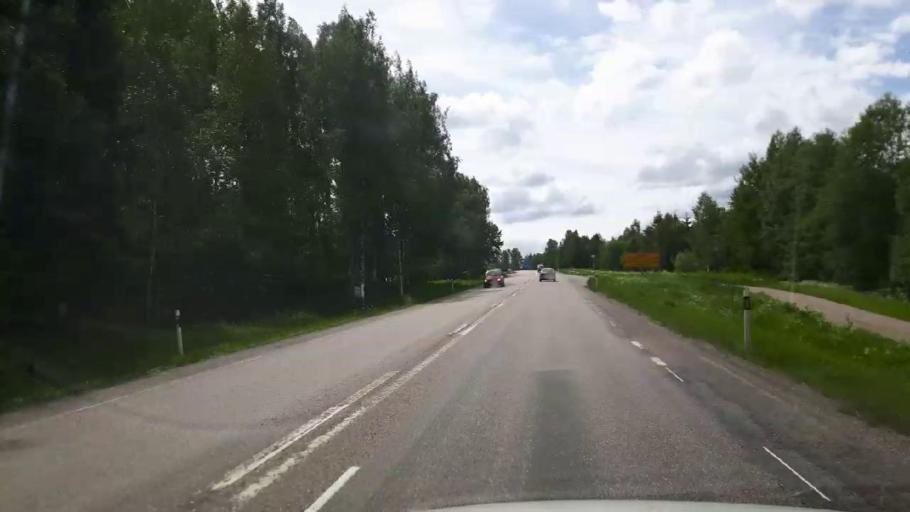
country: SE
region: Vaestmanland
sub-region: Fagersta Kommun
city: Fagersta
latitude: 59.9687
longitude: 15.7725
